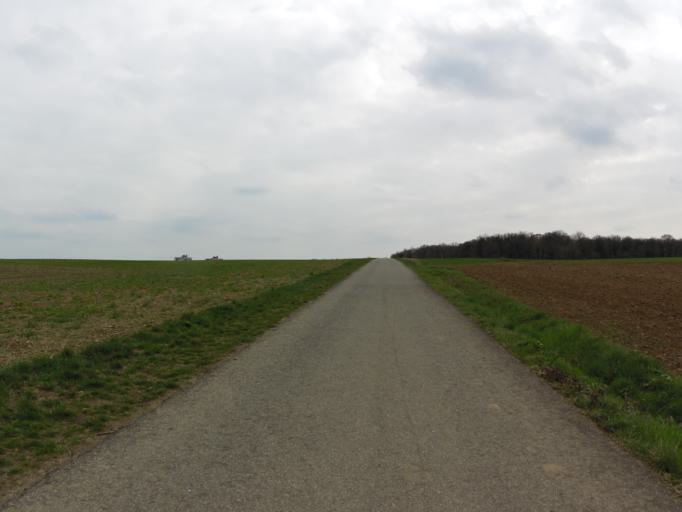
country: DE
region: Bavaria
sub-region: Regierungsbezirk Unterfranken
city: Rottendorf
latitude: 49.8040
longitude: 10.0178
